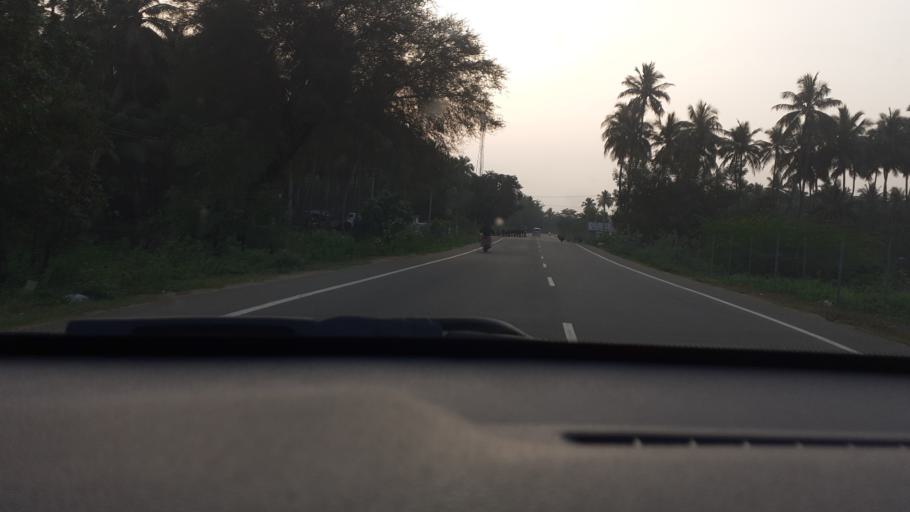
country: IN
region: Tamil Nadu
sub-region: Dindigul
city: Palani
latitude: 10.4323
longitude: 77.5191
